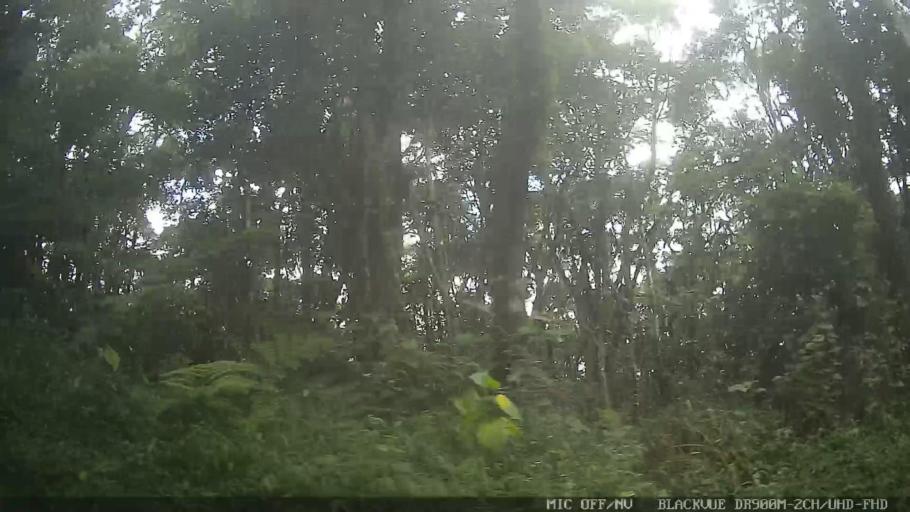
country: BR
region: Minas Gerais
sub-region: Extrema
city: Extrema
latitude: -22.8840
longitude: -46.3143
